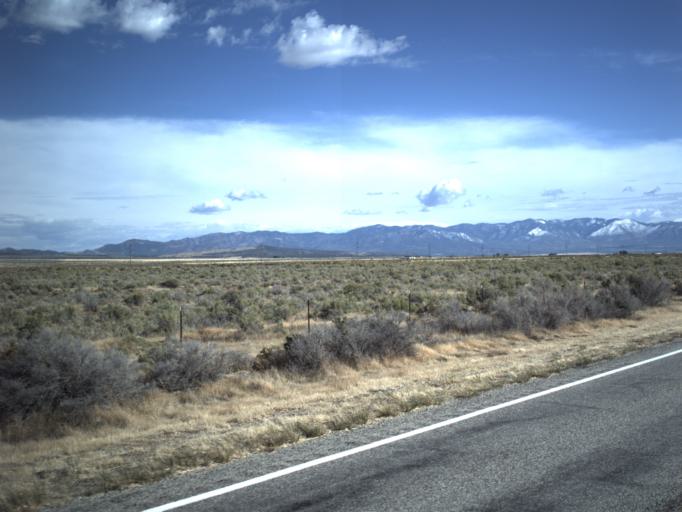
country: US
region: Utah
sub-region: Millard County
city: Delta
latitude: 39.2472
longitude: -112.4374
